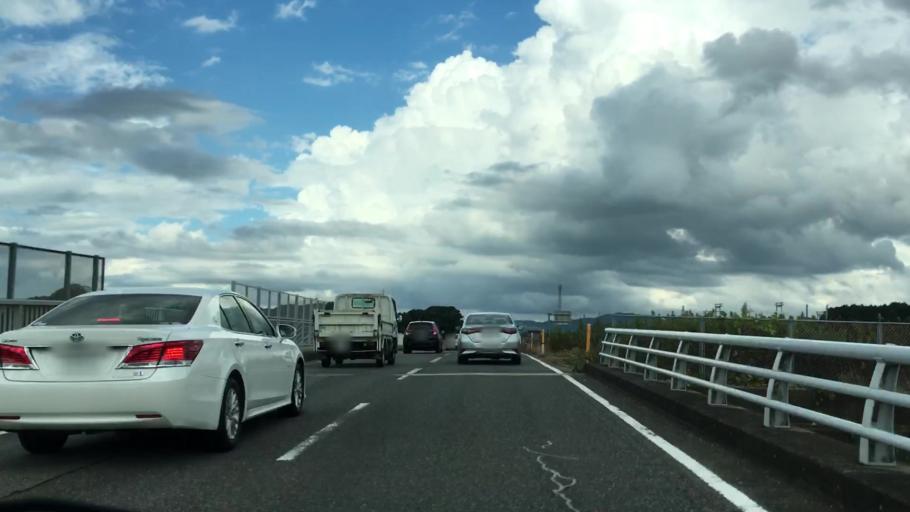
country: JP
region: Fukuoka
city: Maebaru-chuo
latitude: 33.5178
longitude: 130.1559
